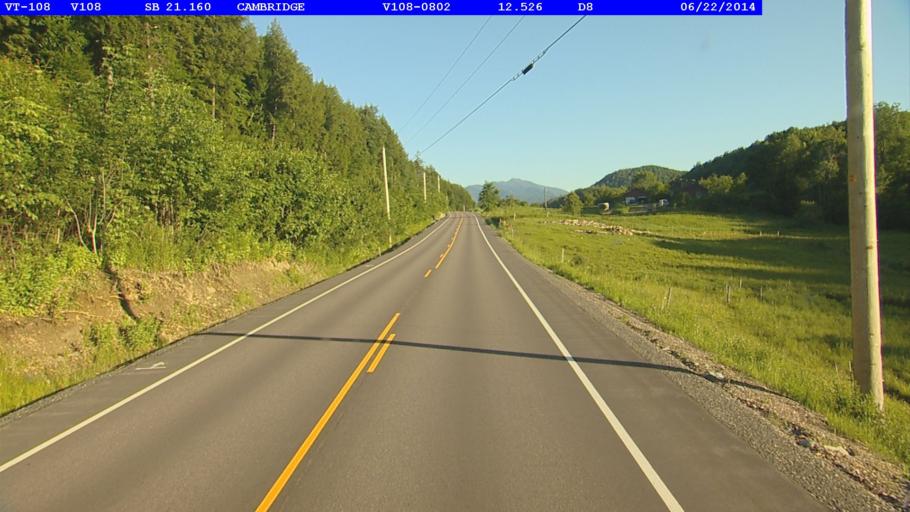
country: US
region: Vermont
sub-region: Lamoille County
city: Johnson
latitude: 44.6956
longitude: -72.8277
